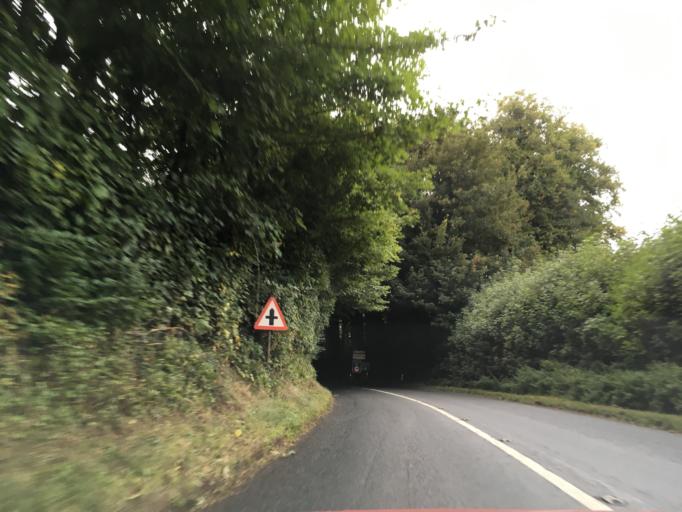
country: GB
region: England
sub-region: Herefordshire
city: Lea
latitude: 51.8871
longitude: -2.4811
